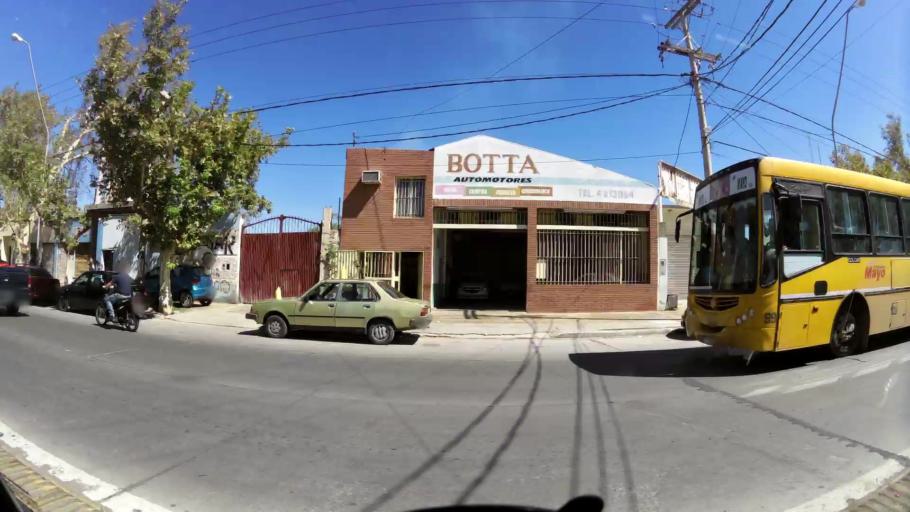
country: AR
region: San Juan
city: Villa Krause
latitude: -31.5603
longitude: -68.5244
